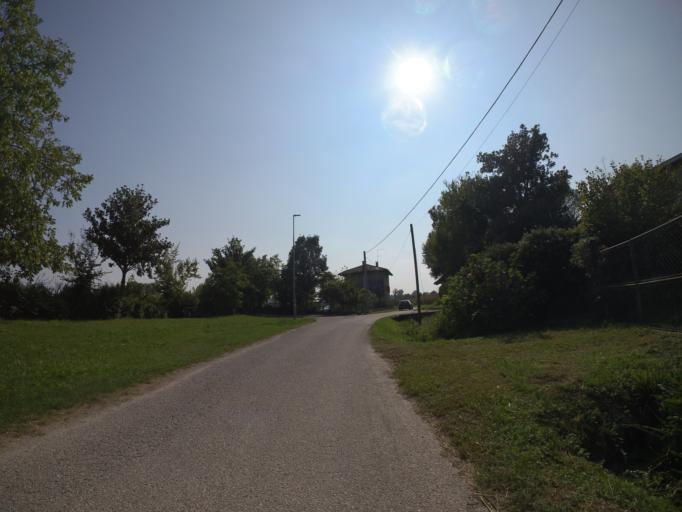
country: IT
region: Friuli Venezia Giulia
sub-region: Provincia di Udine
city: Camino al Tagliamento
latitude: 45.9160
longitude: 12.9295
